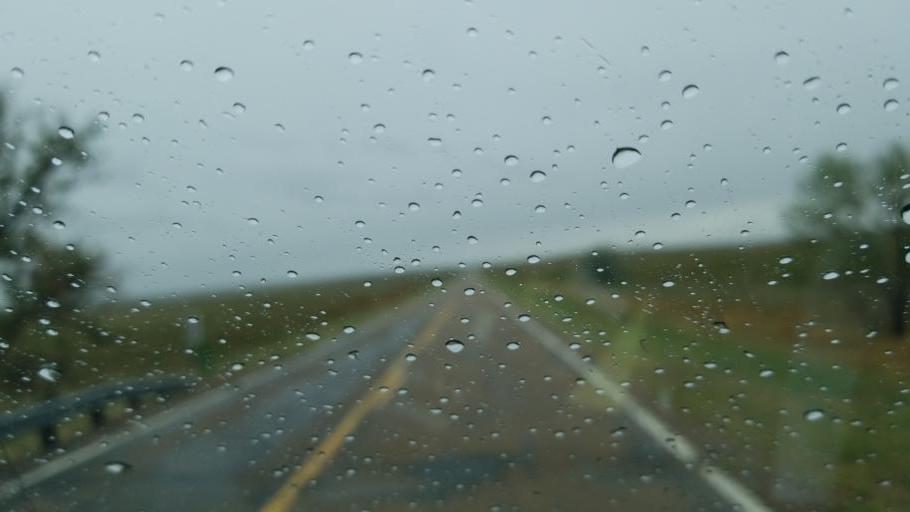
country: US
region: Colorado
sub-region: Lincoln County
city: Hugo
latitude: 38.8596
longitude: -103.1440
